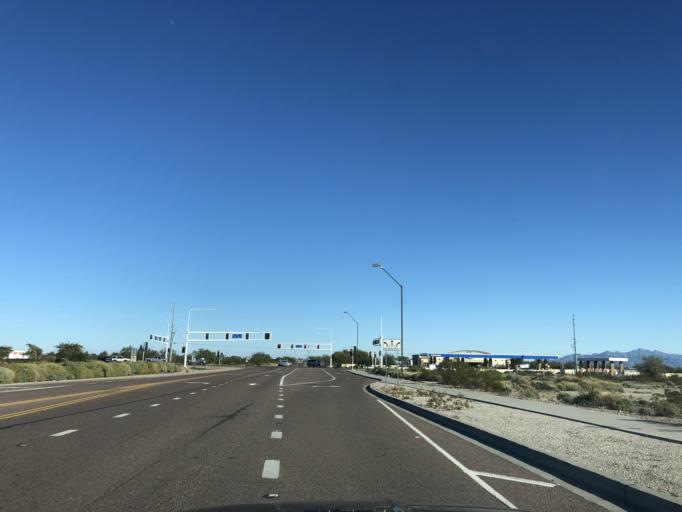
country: US
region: Arizona
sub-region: Maricopa County
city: Buckeye
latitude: 33.4281
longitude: -112.5927
